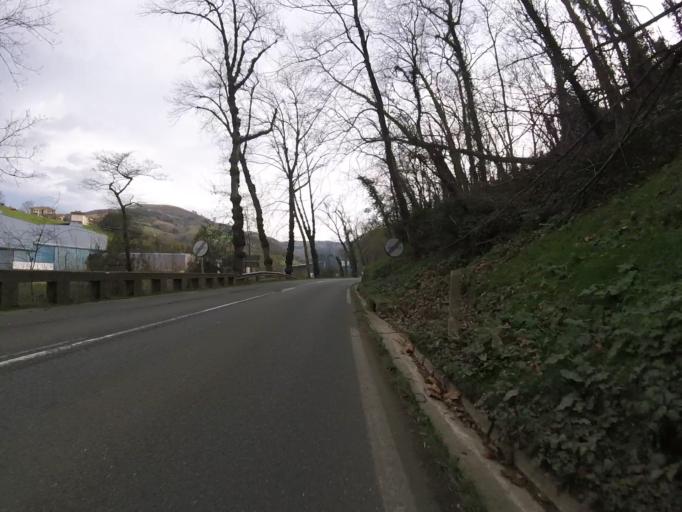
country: ES
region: Basque Country
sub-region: Provincia de Guipuzcoa
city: Aizarnazabal
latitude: 43.2529
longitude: -2.2413
